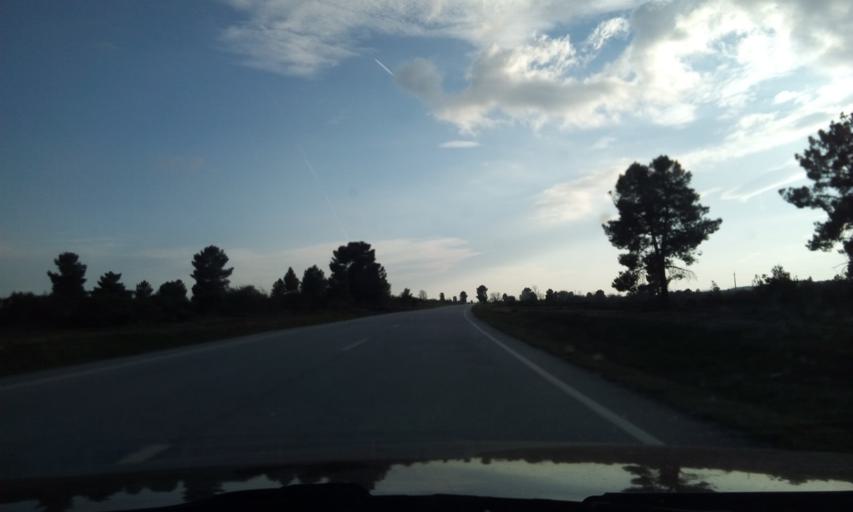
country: ES
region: Castille and Leon
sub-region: Provincia de Salamanca
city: Fuentes de Onoro
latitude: 40.6271
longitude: -6.9741
